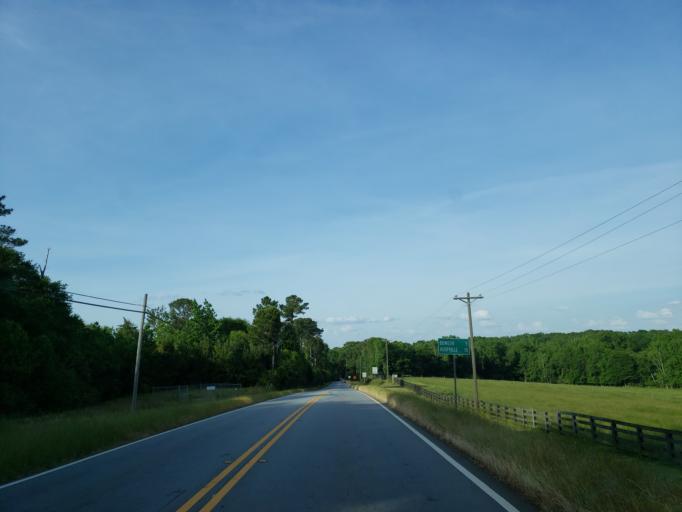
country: US
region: Georgia
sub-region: Carroll County
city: Bowdon
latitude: 33.4709
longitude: -85.2945
